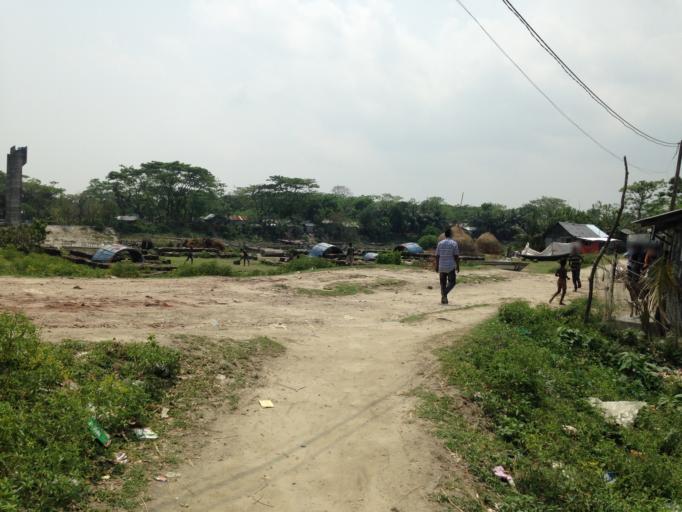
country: BD
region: Chittagong
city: Lakshmipur
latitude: 22.8723
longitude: 90.7844
